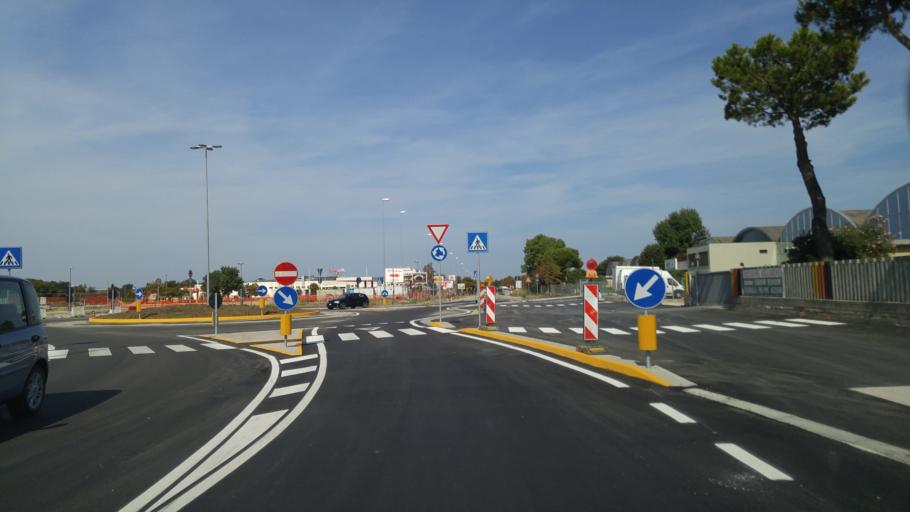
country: IT
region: The Marches
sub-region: Provincia di Pesaro e Urbino
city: Bellocchi
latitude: 43.7976
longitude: 13.0092
